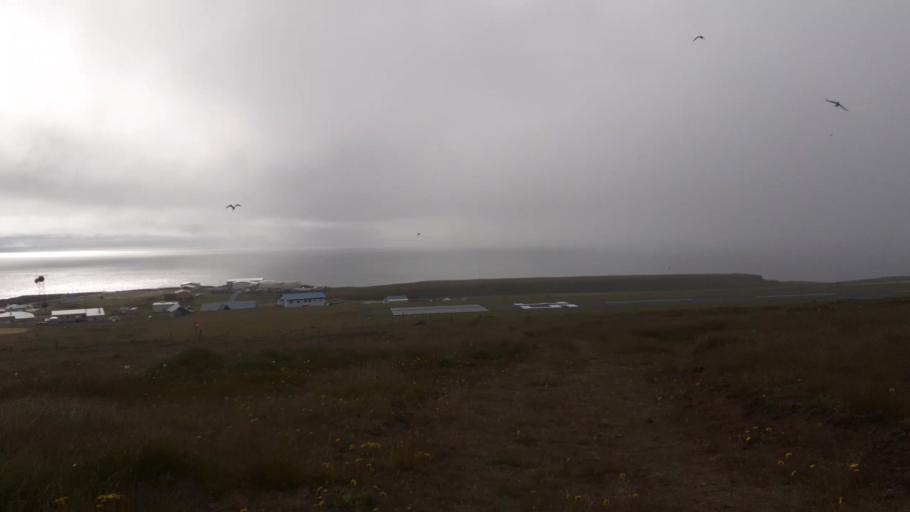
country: IS
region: Northeast
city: Dalvik
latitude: 66.5424
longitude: -18.0083
